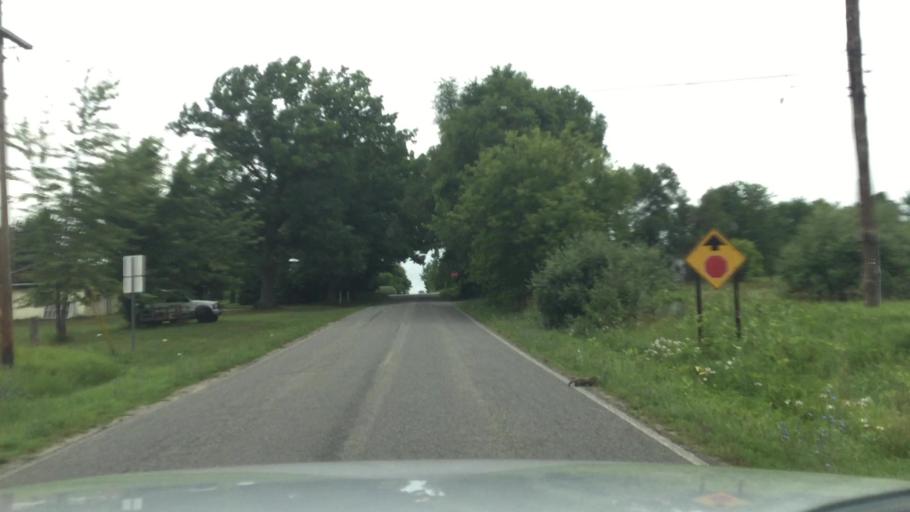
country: US
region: Michigan
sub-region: Montcalm County
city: Greenville
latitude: 43.1910
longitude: -85.2231
